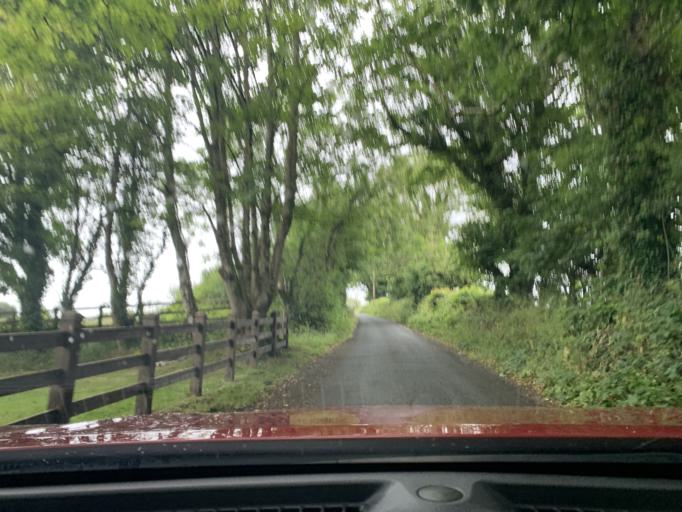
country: IE
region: Connaught
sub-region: Sligo
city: Sligo
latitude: 54.3041
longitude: -8.4565
